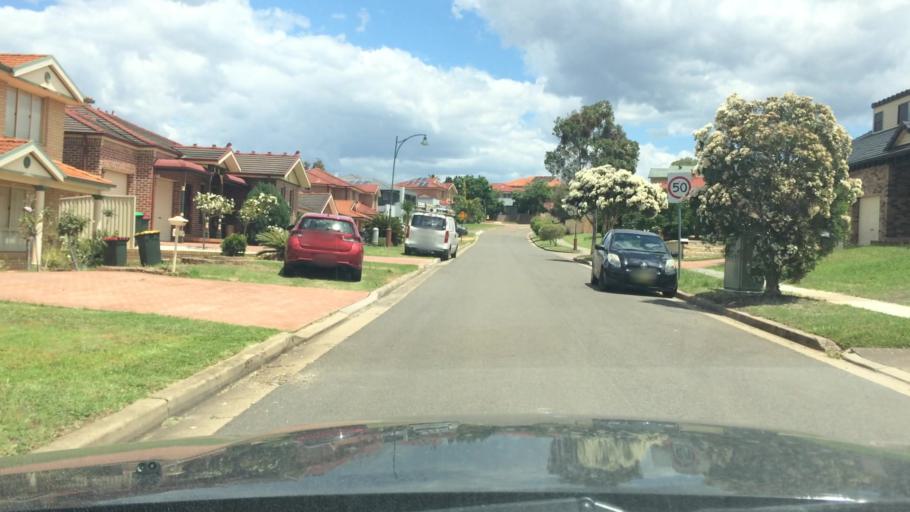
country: AU
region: New South Wales
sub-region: Campbelltown Municipality
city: Denham Court
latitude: -33.9400
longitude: 150.8349
